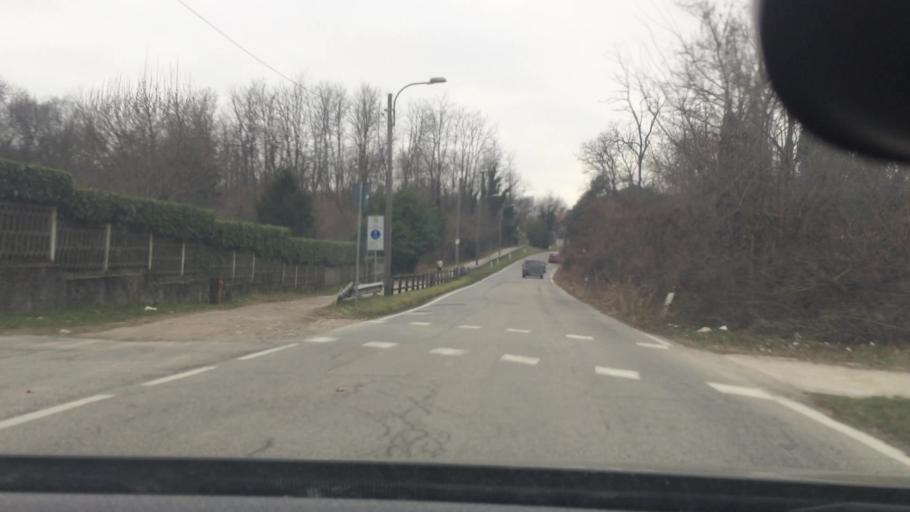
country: IT
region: Lombardy
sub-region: Provincia di Monza e Brianza
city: Villaggio del Sole
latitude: 45.6392
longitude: 9.1081
